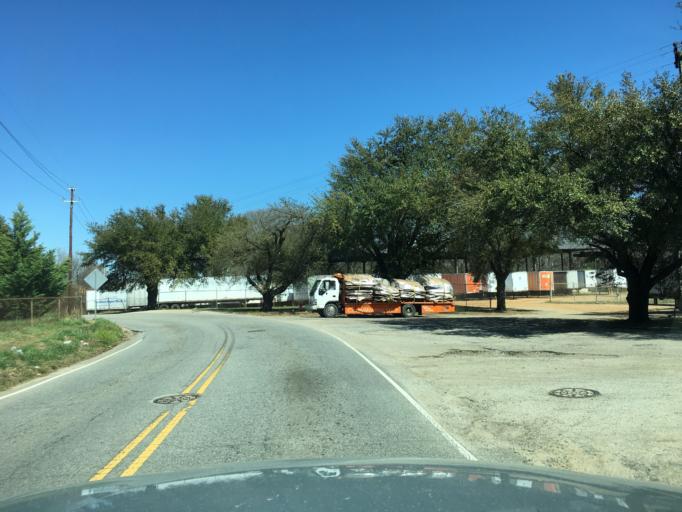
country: US
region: South Carolina
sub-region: Spartanburg County
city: Saxon
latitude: 34.9676
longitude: -81.9669
